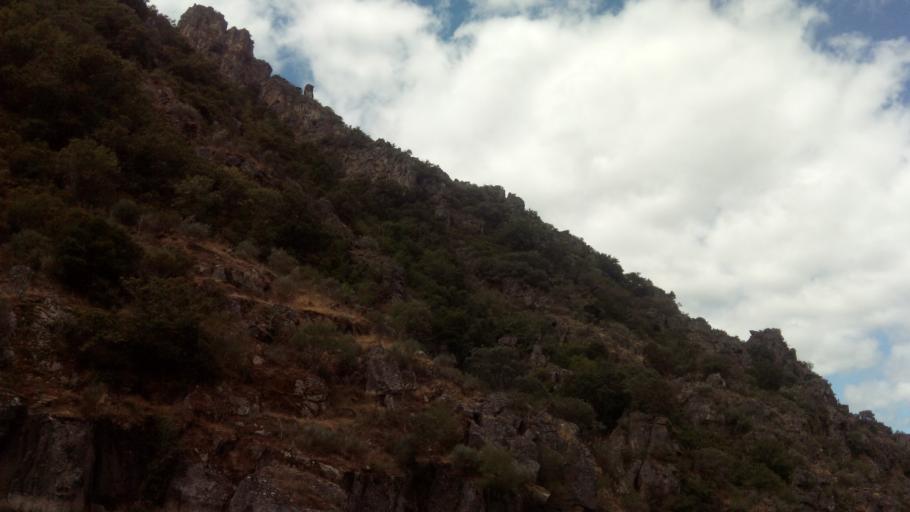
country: ES
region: Galicia
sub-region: Provincia de Lugo
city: Sober
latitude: 42.4029
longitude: -7.6298
